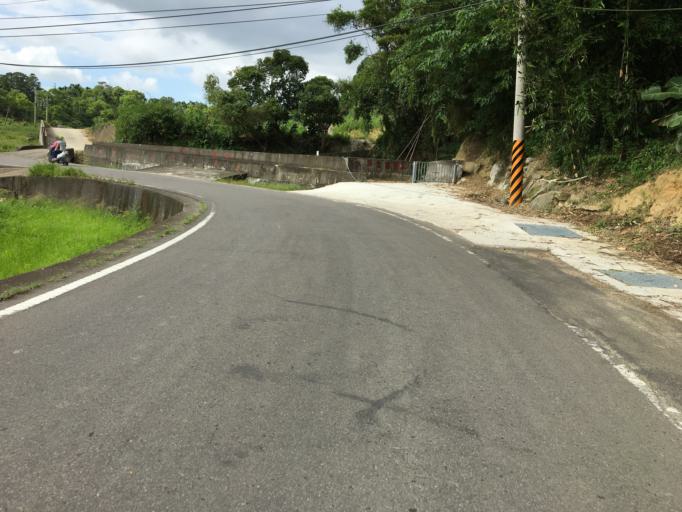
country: TW
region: Taiwan
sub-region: Hsinchu
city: Hsinchu
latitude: 24.7031
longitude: 120.9567
